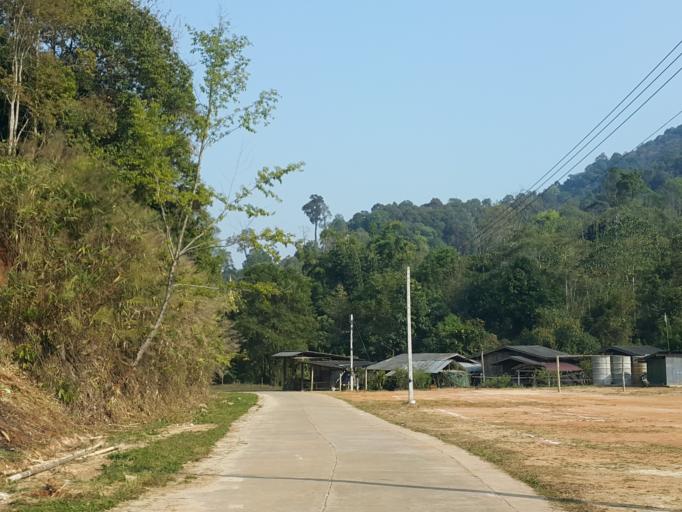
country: TH
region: Chiang Mai
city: Samoeng
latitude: 19.0177
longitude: 98.7591
